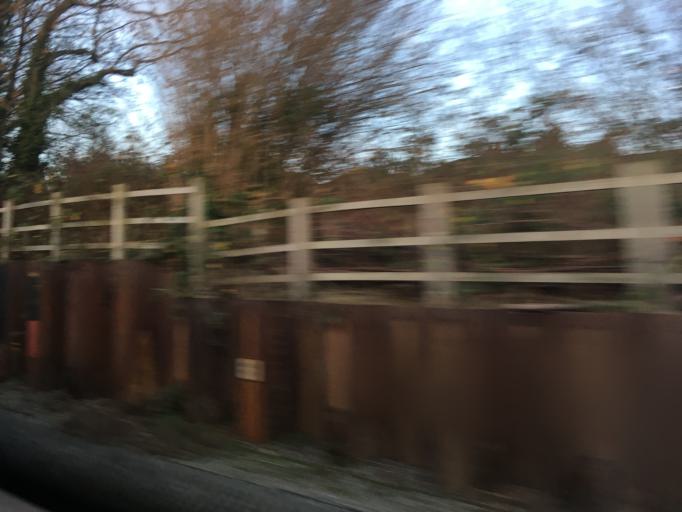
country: GB
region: England
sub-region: Manchester
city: Chorlton cum Hardy
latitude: 53.4441
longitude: -2.2748
